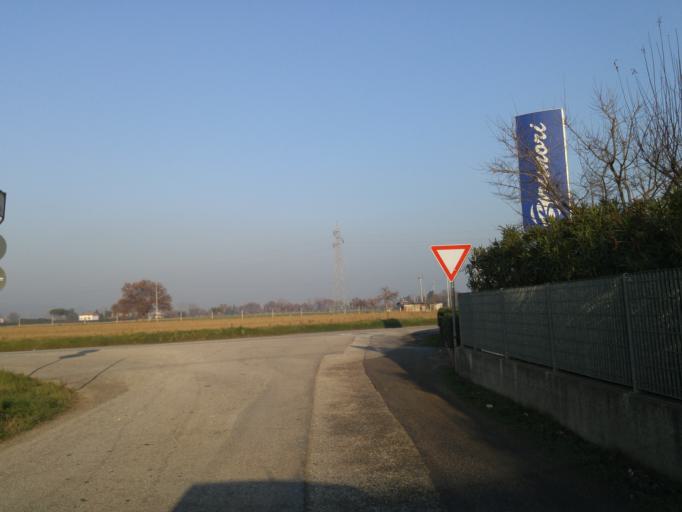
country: IT
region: The Marches
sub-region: Provincia di Pesaro e Urbino
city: Lucrezia
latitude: 43.7712
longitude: 12.9536
